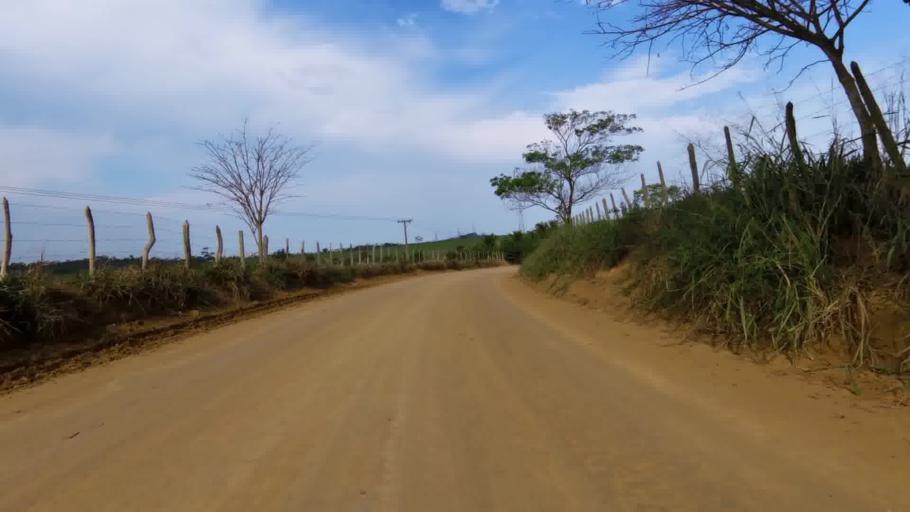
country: BR
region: Espirito Santo
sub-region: Piuma
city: Piuma
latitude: -20.8287
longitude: -40.7416
